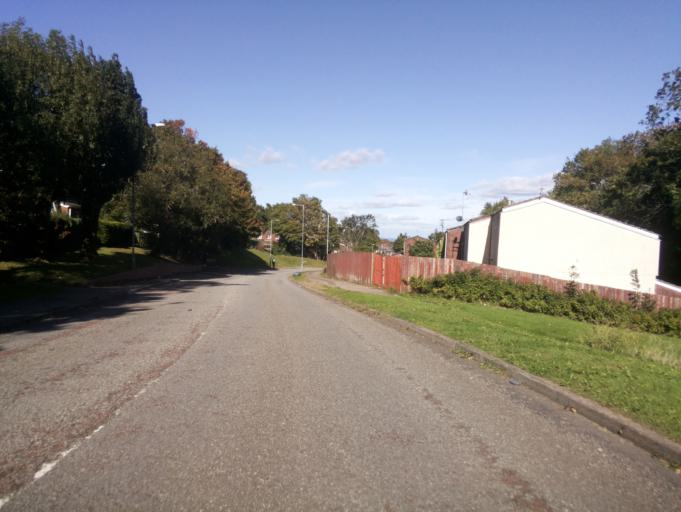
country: GB
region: Wales
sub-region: Torfaen County Borough
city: Cwmbran
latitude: 51.6590
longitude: -3.0482
